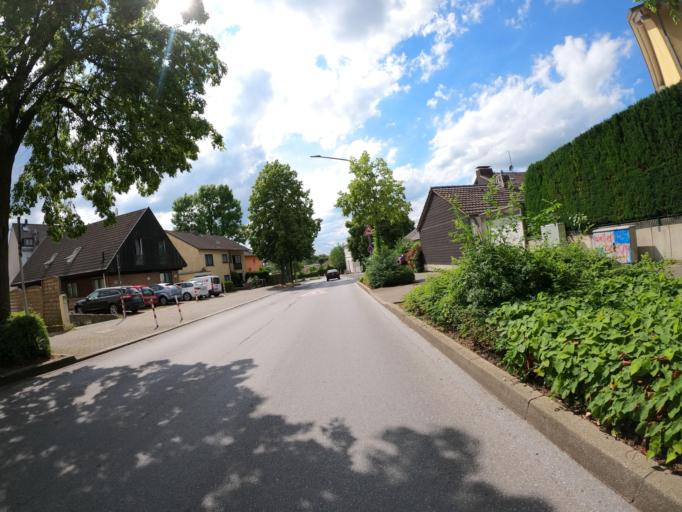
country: DE
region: North Rhine-Westphalia
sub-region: Regierungsbezirk Dusseldorf
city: Wuppertal
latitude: 51.2516
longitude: 7.1145
